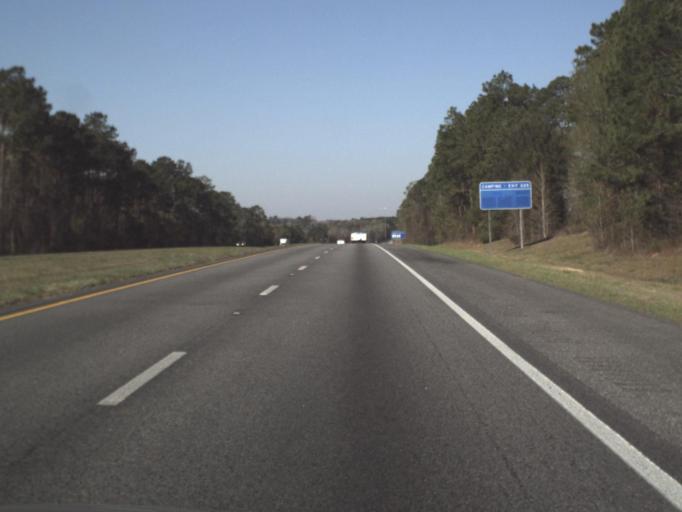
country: US
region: Florida
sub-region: Jefferson County
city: Monticello
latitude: 30.4735
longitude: -83.8717
